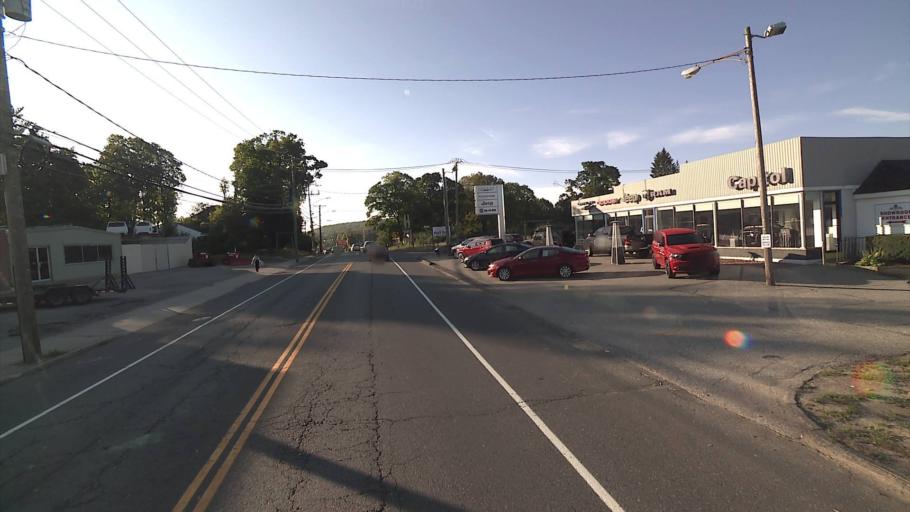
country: US
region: Connecticut
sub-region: Windham County
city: Willimantic
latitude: 41.7187
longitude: -72.2354
